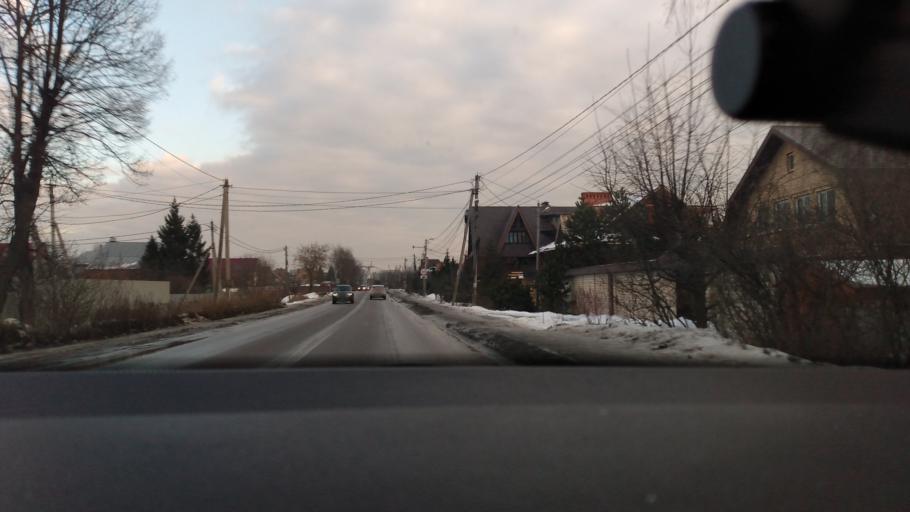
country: RU
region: Moskovskaya
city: Chornaya
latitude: 55.7054
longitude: 38.0518
